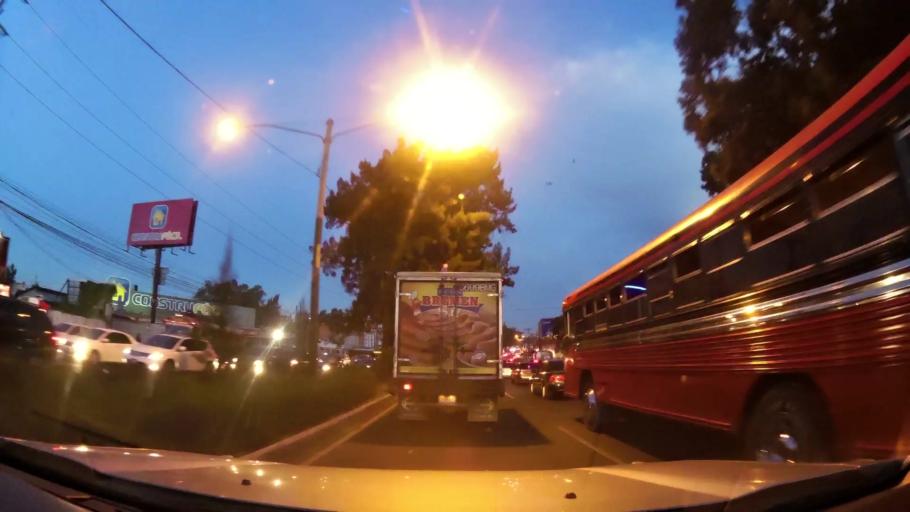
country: GT
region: Guatemala
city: Mixco
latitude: 14.6338
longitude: -90.5735
